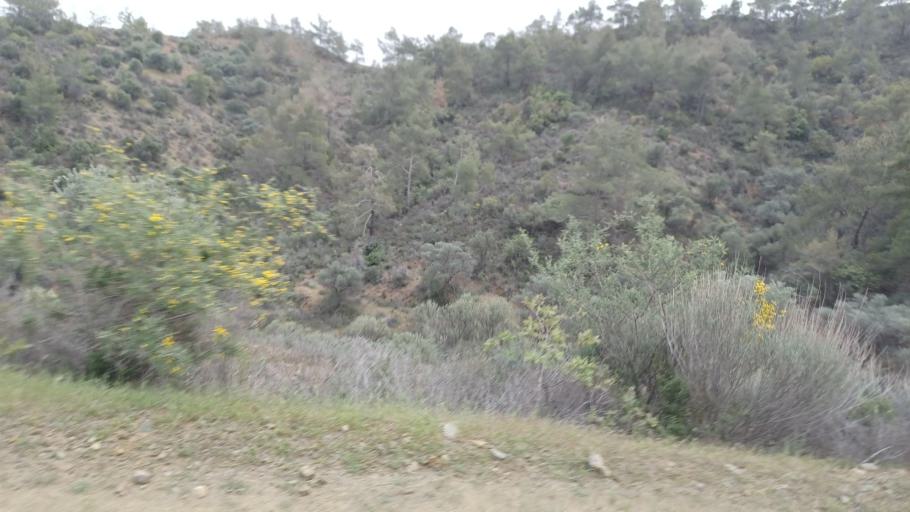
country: CY
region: Limassol
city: Parekklisha
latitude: 34.8586
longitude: 33.1072
